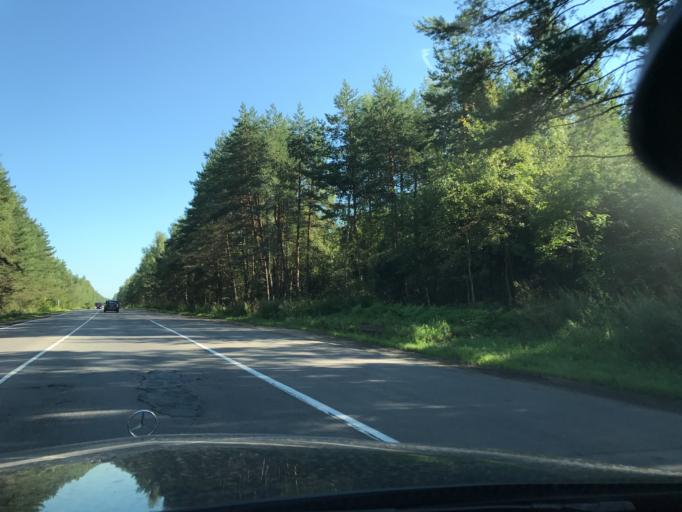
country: RU
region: Moskovskaya
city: Noginsk-9
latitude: 56.0833
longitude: 38.5768
